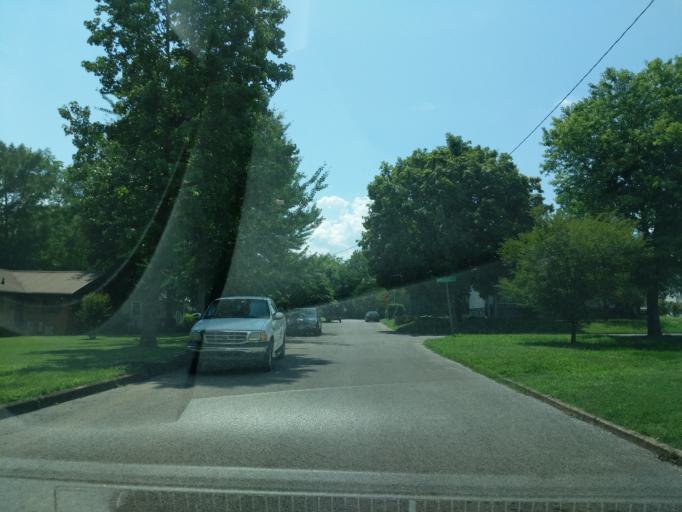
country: US
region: Tennessee
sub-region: Davidson County
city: Lakewood
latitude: 36.2554
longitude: -86.6441
